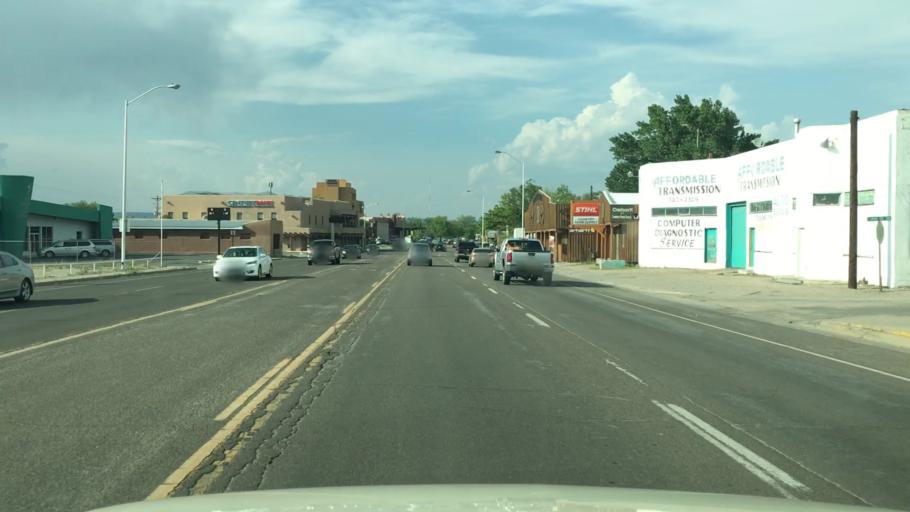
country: US
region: New Mexico
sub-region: Rio Arriba County
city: Espanola
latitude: 35.9929
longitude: -106.0680
